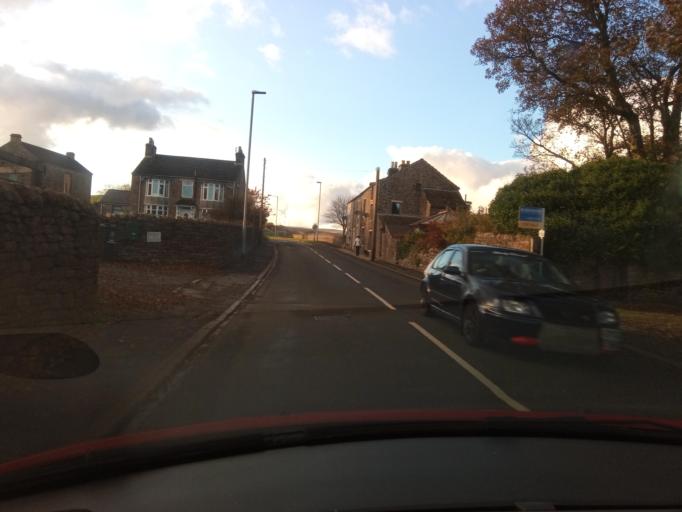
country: GB
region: England
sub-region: County Durham
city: Newbiggin
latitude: 54.7392
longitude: -2.1881
